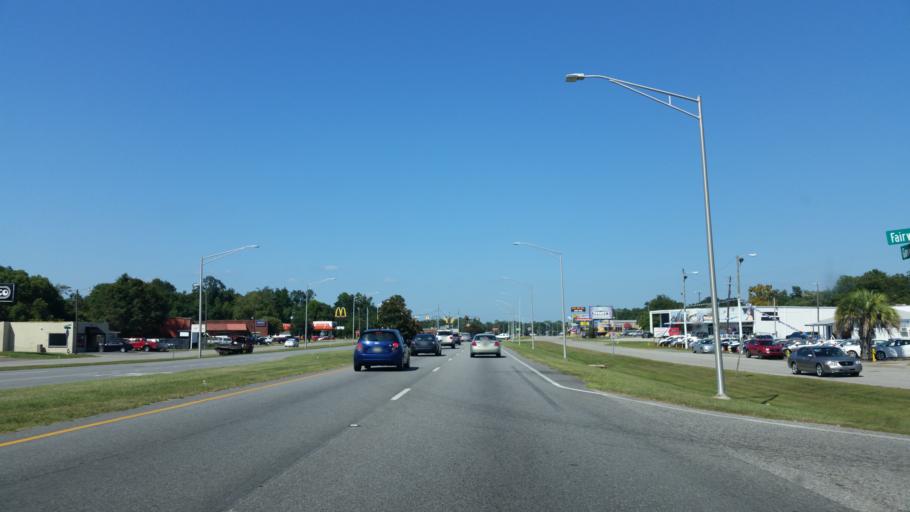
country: US
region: Alabama
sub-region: Mobile County
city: Mobile
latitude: 30.6635
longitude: -88.1069
